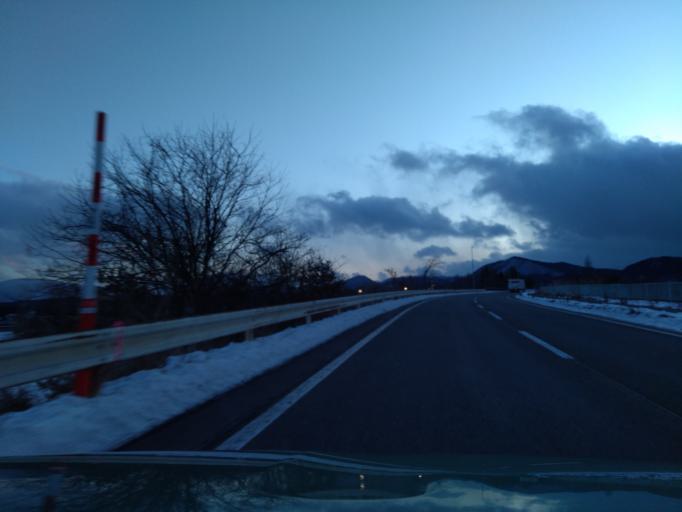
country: JP
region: Iwate
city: Shizukuishi
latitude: 39.6944
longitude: 140.9359
